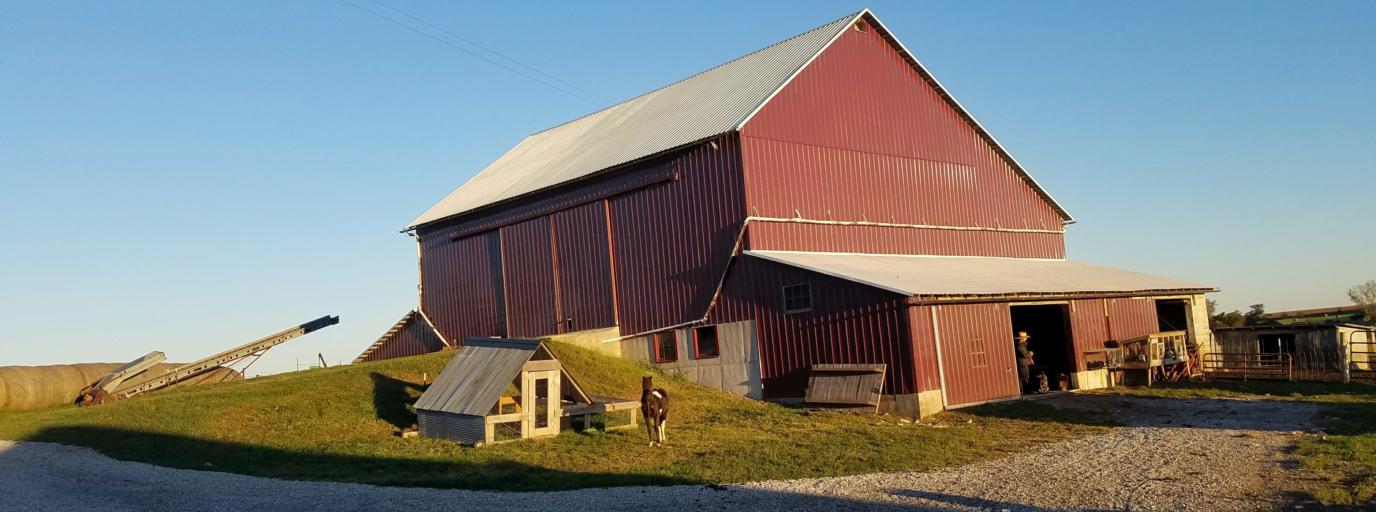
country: US
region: Iowa
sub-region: Decatur County
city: Lamoni
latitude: 40.5851
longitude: -93.9398
